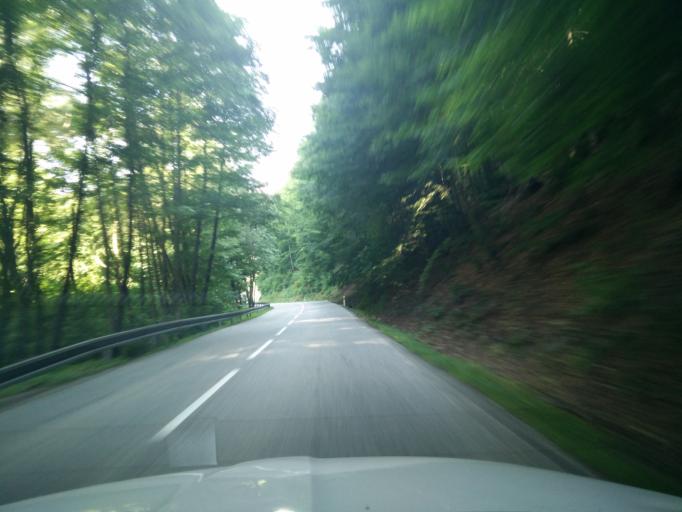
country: SK
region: Nitriansky
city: Bojnice
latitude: 48.8409
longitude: 18.4710
